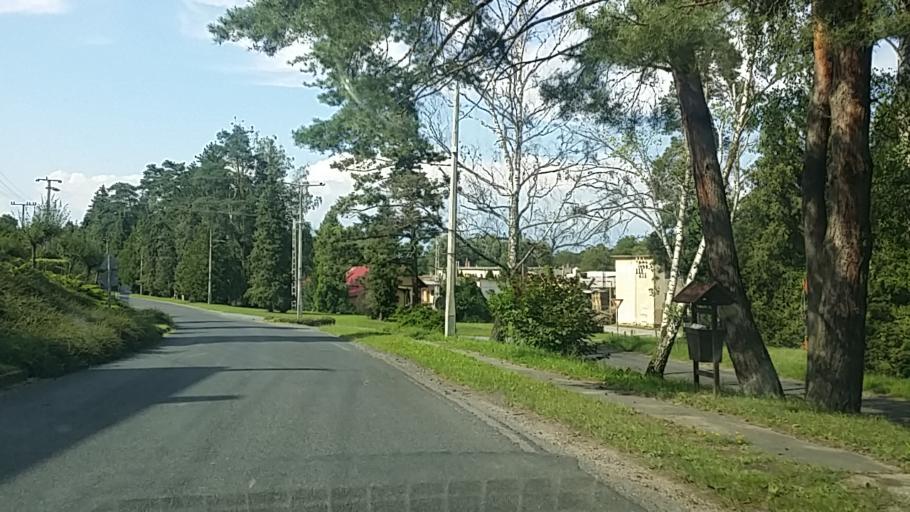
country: HU
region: Zala
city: Becsehely
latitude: 46.5229
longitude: 16.7288
